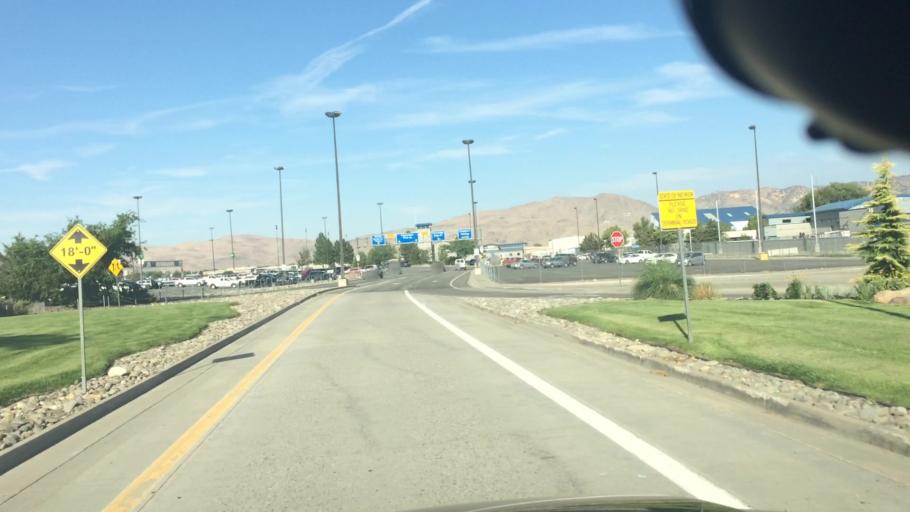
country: US
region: Nevada
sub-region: Washoe County
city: Sparks
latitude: 39.5017
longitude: -119.7791
